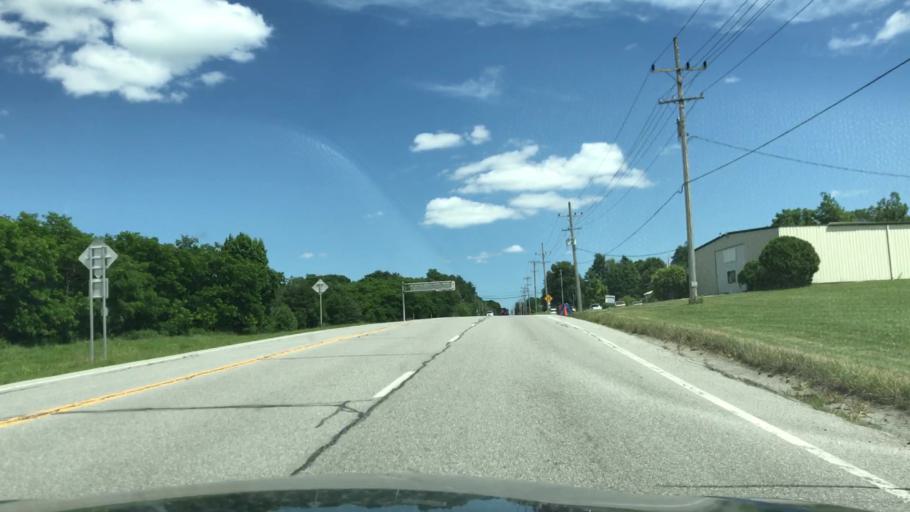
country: US
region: New York
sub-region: Wyoming County
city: Warsaw
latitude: 42.7465
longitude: -78.1225
